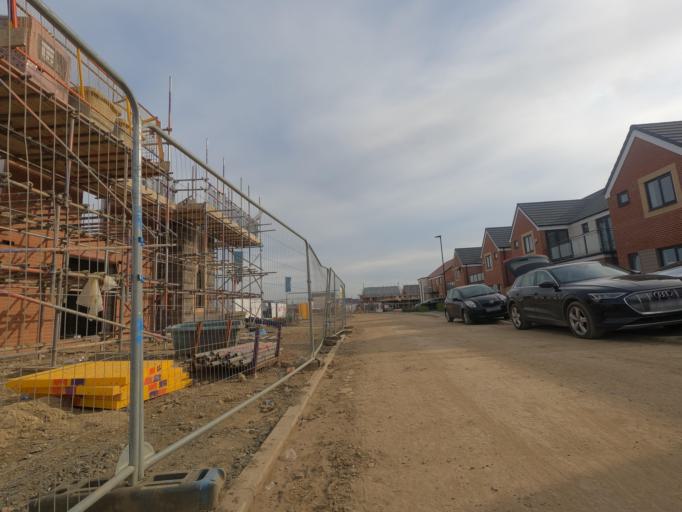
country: GB
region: England
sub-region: Newcastle upon Tyne
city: Hazlerigg
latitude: 55.0314
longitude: -1.6568
